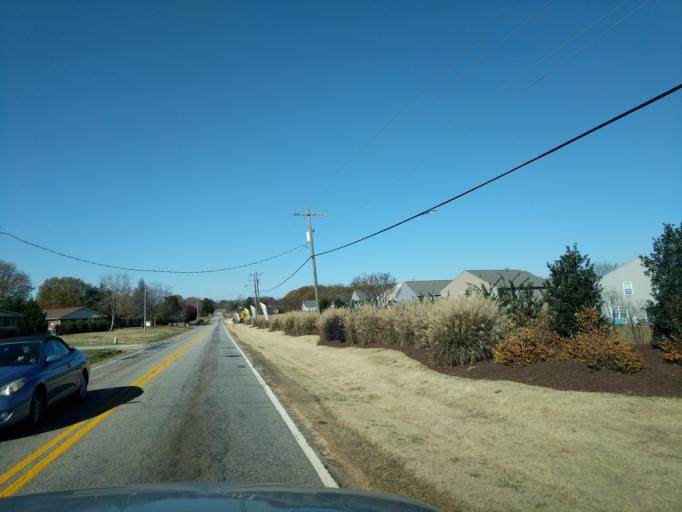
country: US
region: South Carolina
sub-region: Spartanburg County
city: Lyman
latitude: 34.9649
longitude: -82.1410
